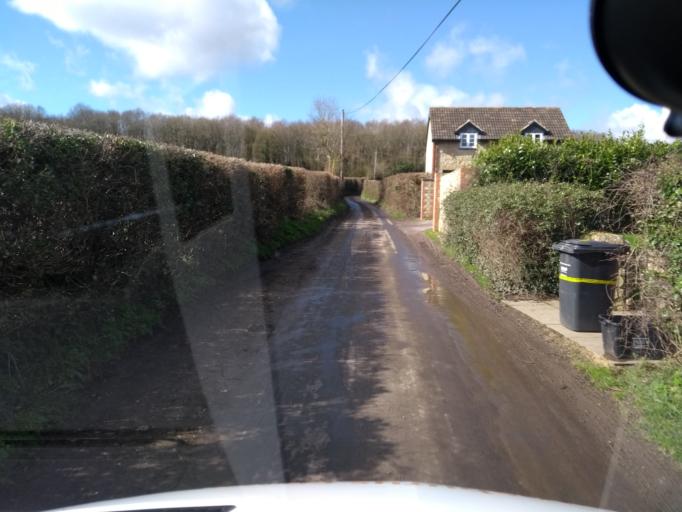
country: GB
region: England
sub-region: Somerset
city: Creech Saint Michael
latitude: 50.9723
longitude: -3.0465
